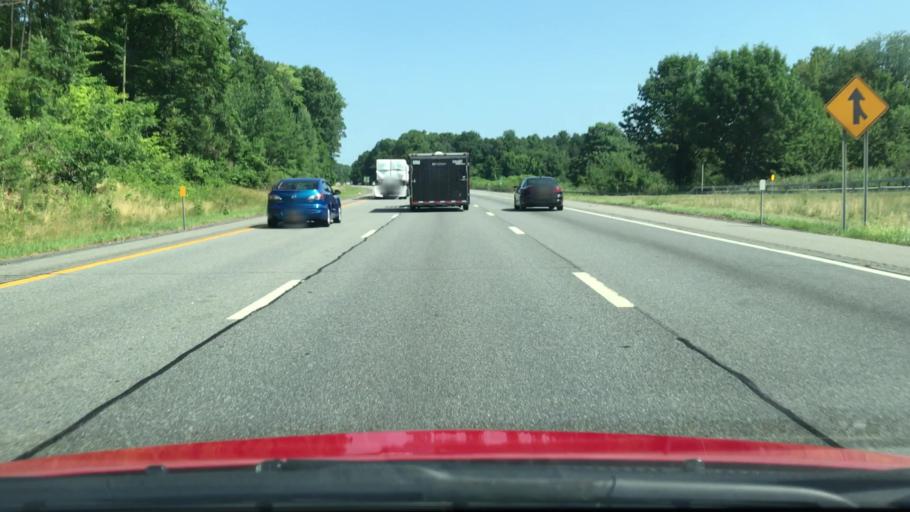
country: US
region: New York
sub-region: Albany County
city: Cohoes
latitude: 42.8205
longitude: -73.7673
